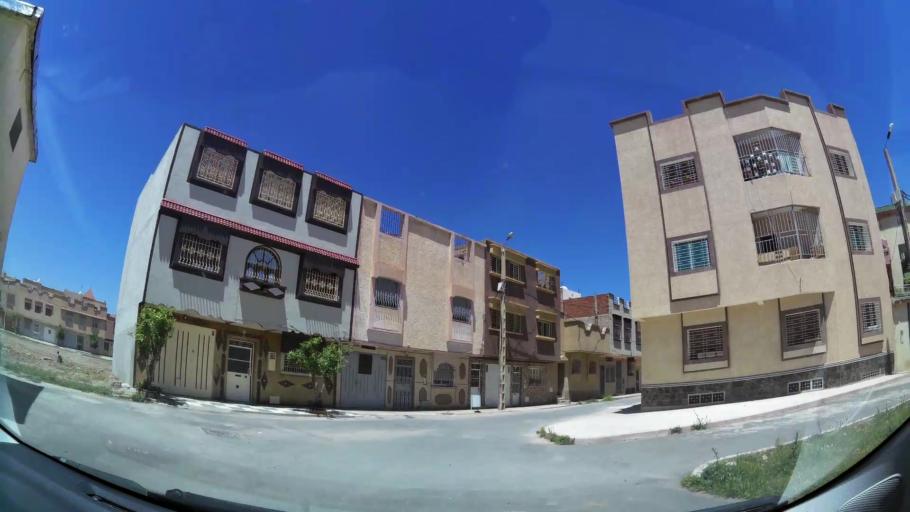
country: MA
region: Oriental
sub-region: Oujda-Angad
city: Oujda
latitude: 34.6807
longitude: -1.8738
